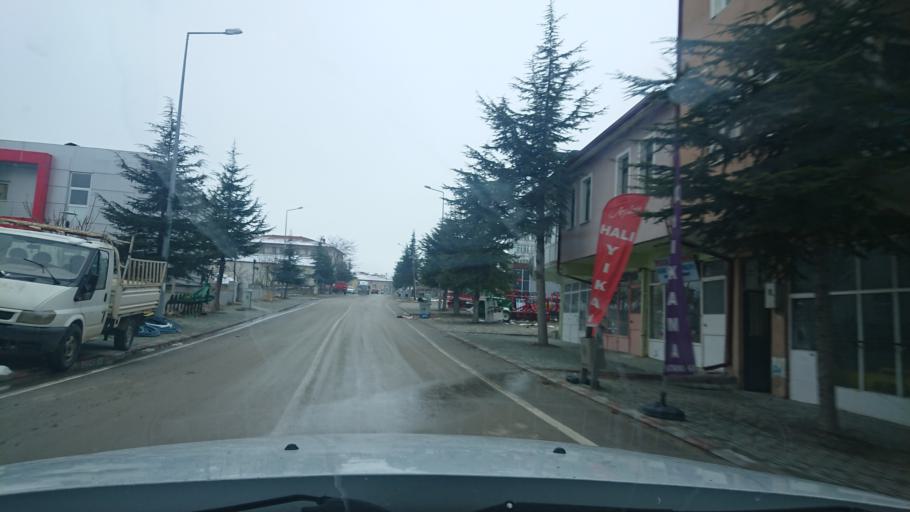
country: TR
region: Aksaray
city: Agacoren
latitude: 38.8706
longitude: 33.9141
